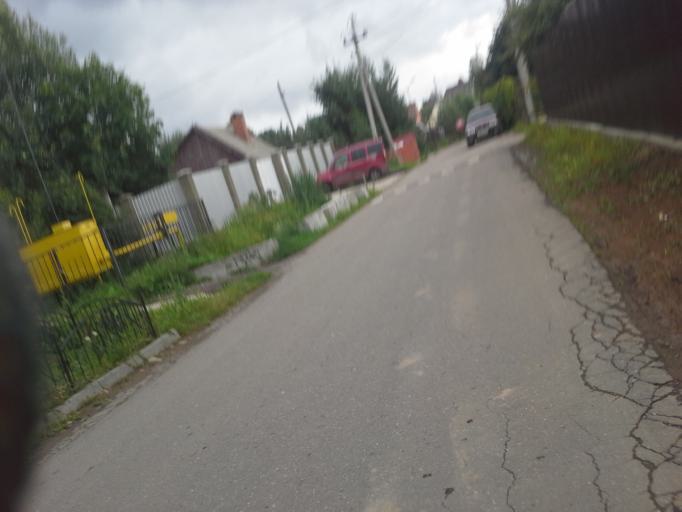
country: RU
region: Moskovskaya
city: Odintsovo
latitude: 55.6458
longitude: 37.2600
